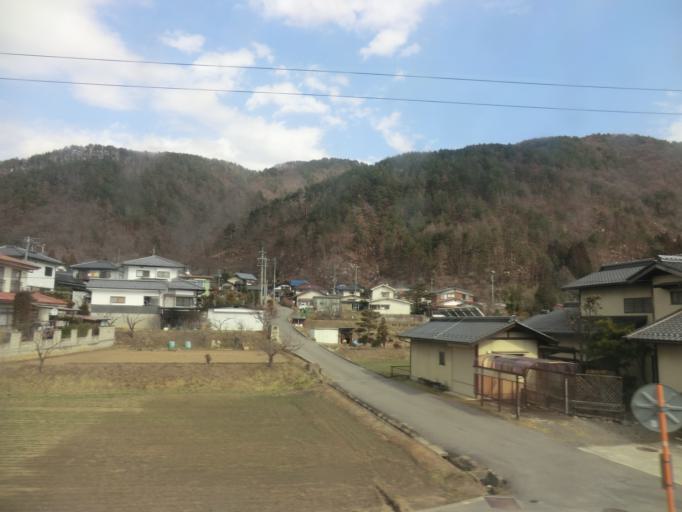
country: JP
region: Nagano
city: Toyoshina
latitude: 36.3325
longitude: 137.9273
